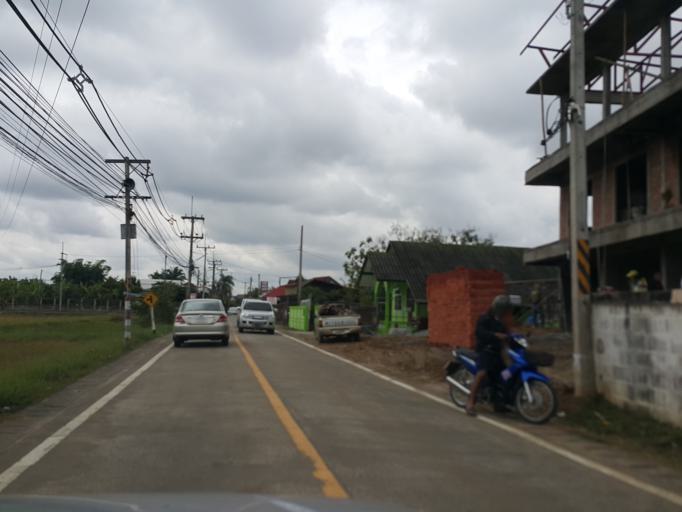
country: TH
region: Lamphun
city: Lamphun
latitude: 18.5722
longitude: 99.0678
